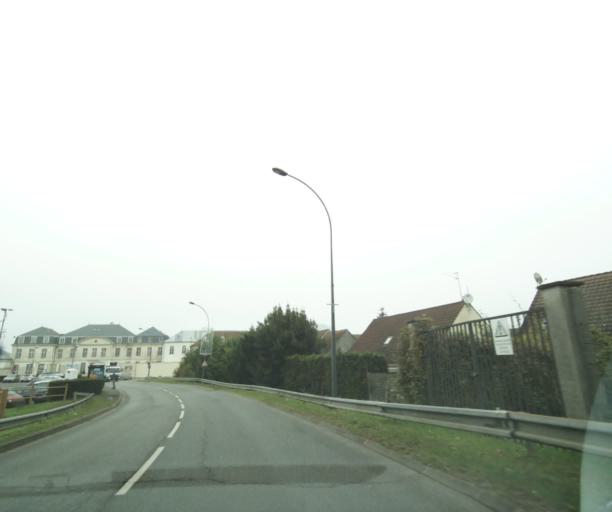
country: FR
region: Ile-de-France
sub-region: Departement de Seine-Saint-Denis
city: Vaujours
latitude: 48.9294
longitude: 2.5701
